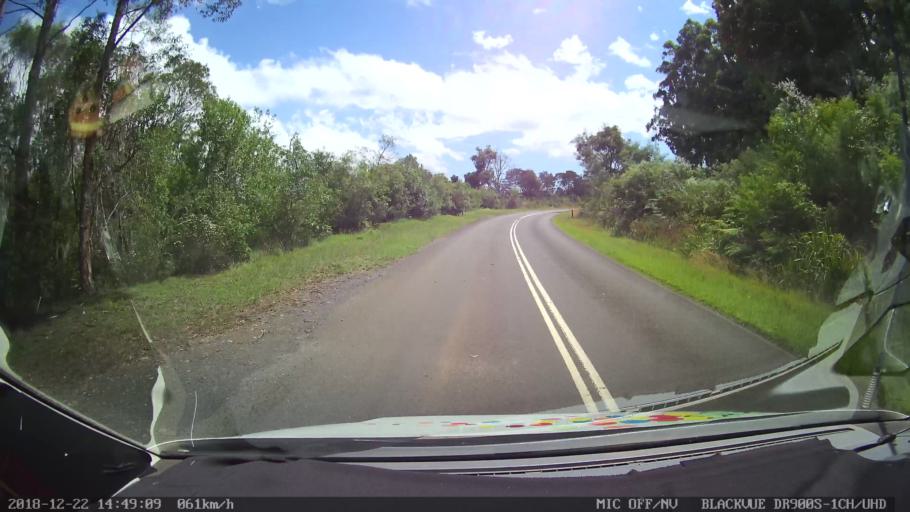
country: AU
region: New South Wales
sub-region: Bellingen
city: Dorrigo
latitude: -30.1872
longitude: 152.5505
